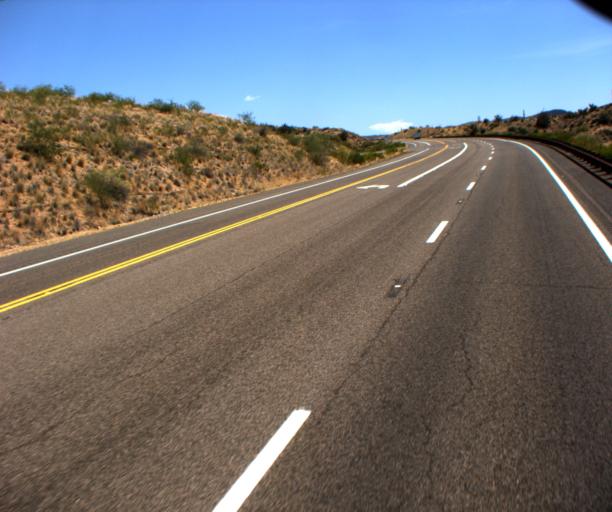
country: US
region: Arizona
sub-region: Gila County
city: Miami
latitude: 33.5667
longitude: -110.9537
